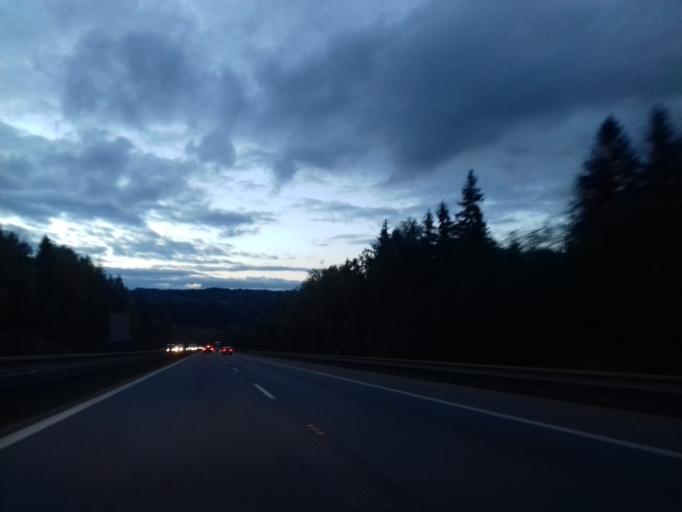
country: CZ
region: Central Bohemia
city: Divisov
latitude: 49.7700
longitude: 14.9449
